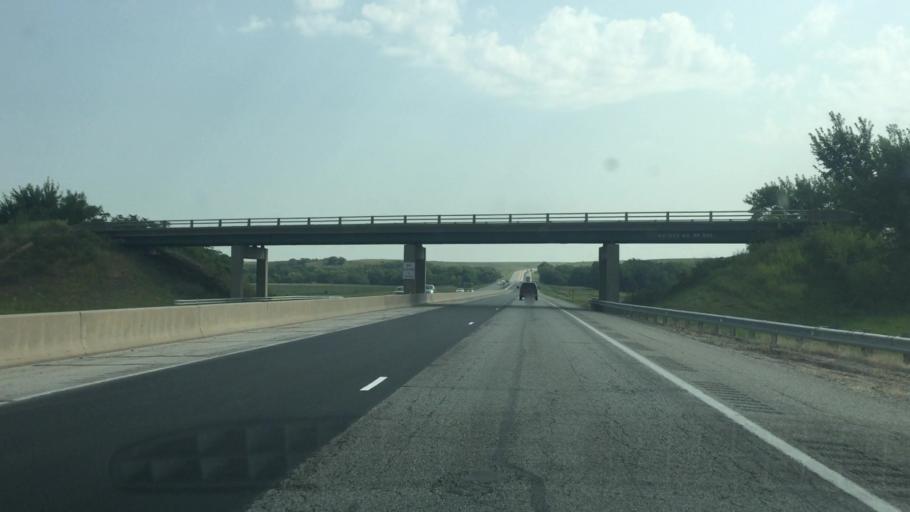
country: US
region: Kansas
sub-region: Chase County
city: Cottonwood Falls
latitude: 38.1237
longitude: -96.5542
